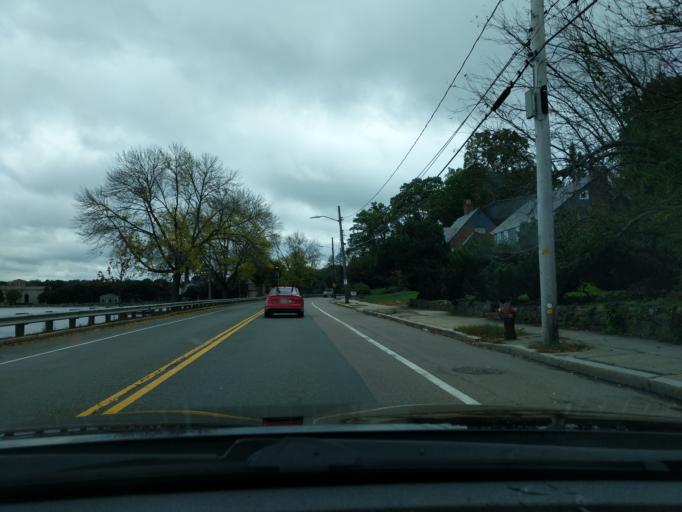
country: US
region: Massachusetts
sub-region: Norfolk County
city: Brookline
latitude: 42.3334
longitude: -71.1606
